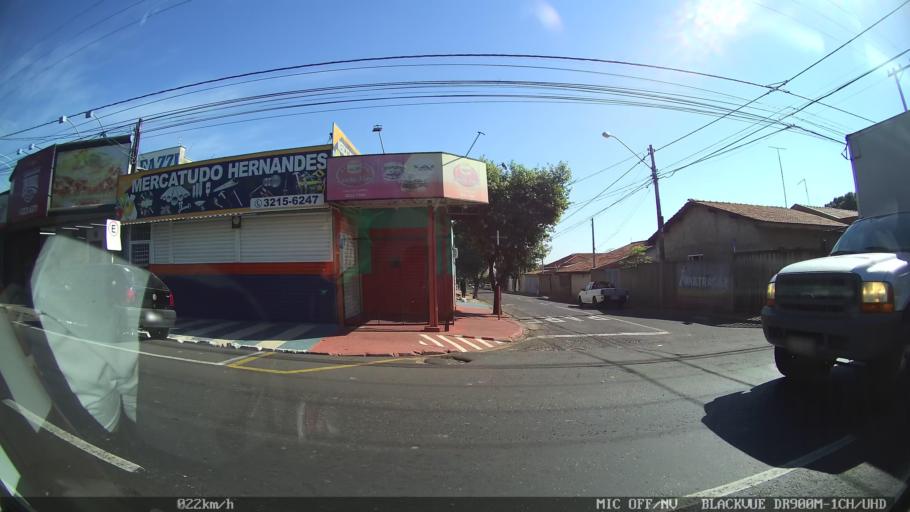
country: BR
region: Sao Paulo
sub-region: Sao Jose Do Rio Preto
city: Sao Jose do Rio Preto
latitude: -20.7744
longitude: -49.3649
